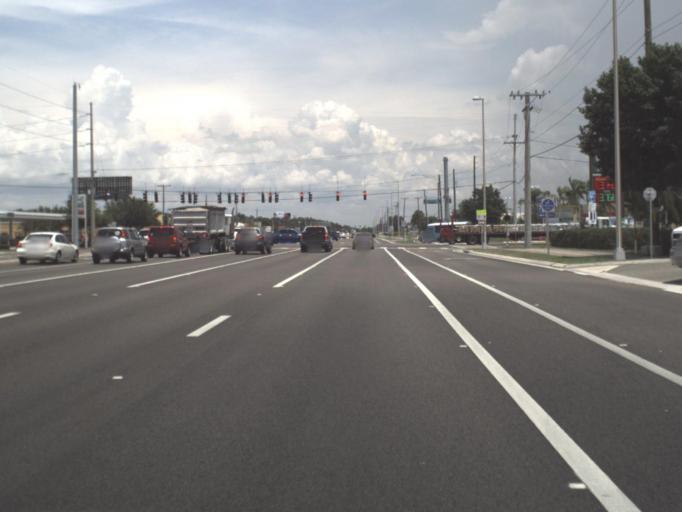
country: US
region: Florida
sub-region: Hillsborough County
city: Sun City Center
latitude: 27.7910
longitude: -82.3347
